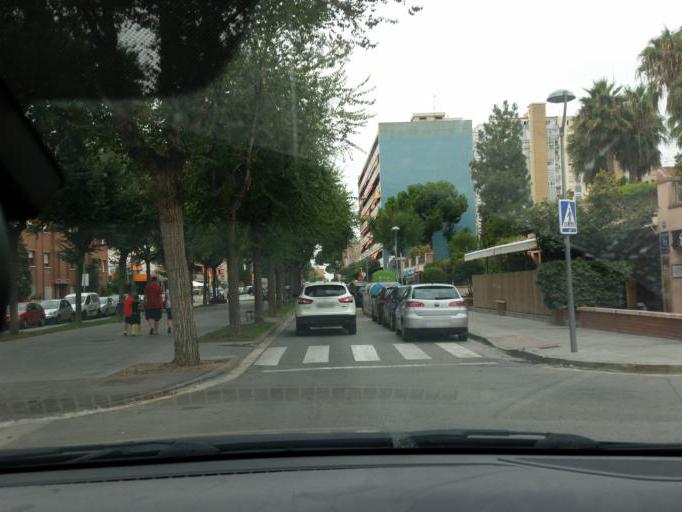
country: ES
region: Catalonia
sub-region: Provincia de Barcelona
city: Vilassar de Mar
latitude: 41.5075
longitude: 2.3900
